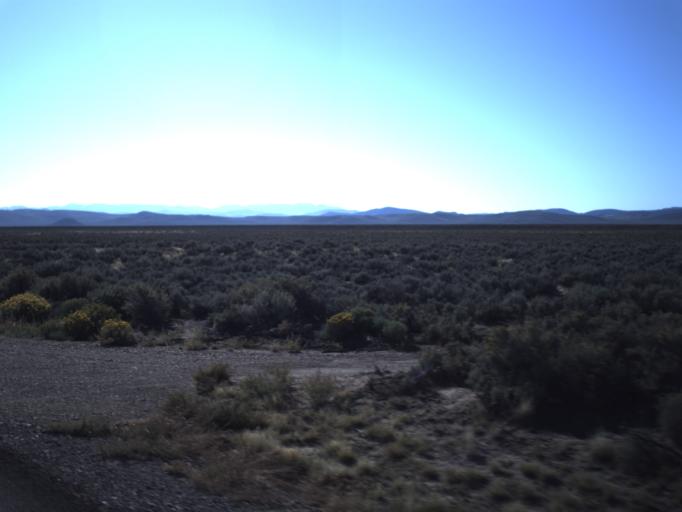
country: US
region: Utah
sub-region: Washington County
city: Enterprise
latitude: 37.7758
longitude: -113.8448
